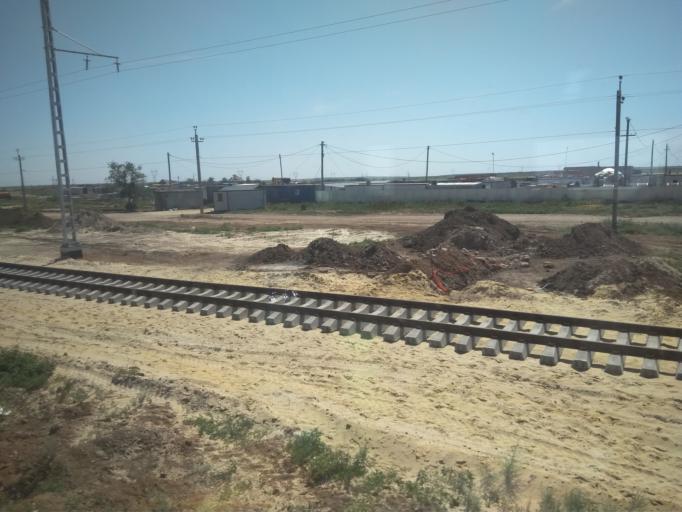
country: RU
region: Volgograd
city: Bereslavka
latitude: 48.2849
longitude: 44.2699
